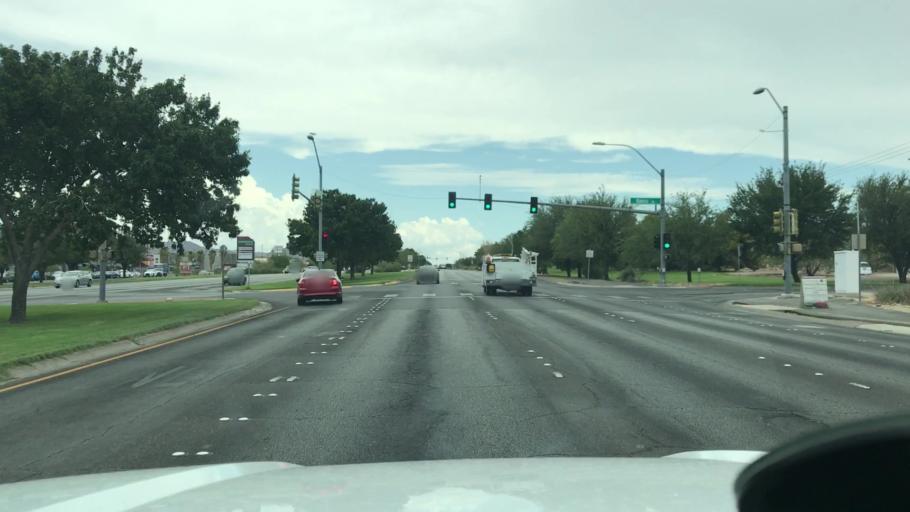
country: US
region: Nevada
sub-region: Clark County
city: Henderson
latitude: 36.0334
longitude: -114.9752
